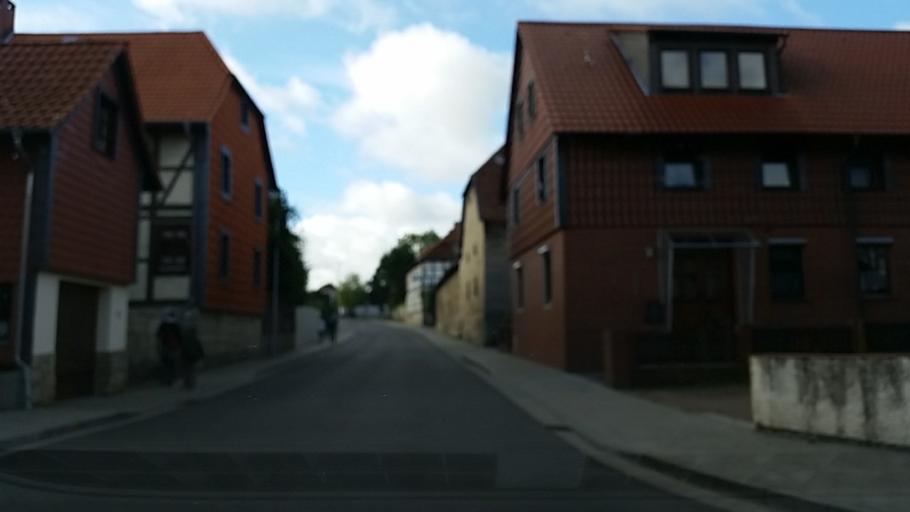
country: DE
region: Lower Saxony
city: Cremlingen
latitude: 52.2474
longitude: 10.6544
